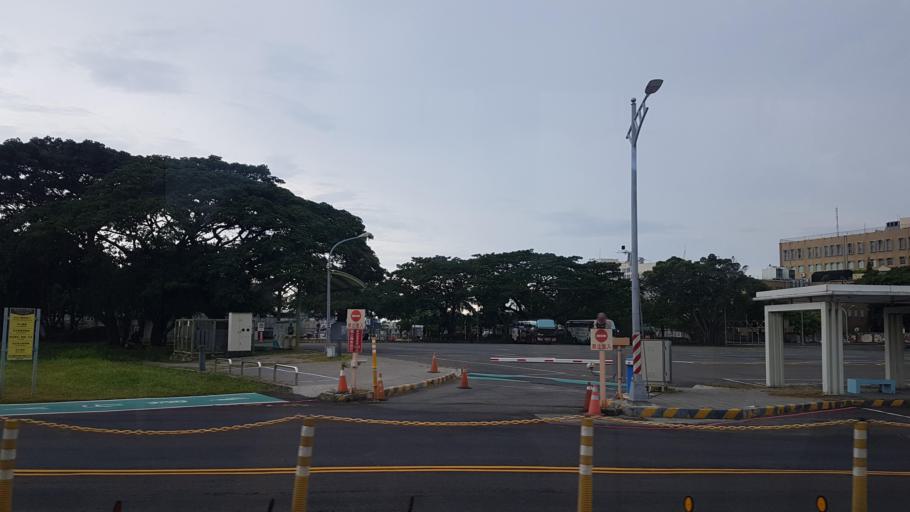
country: TW
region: Kaohsiung
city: Kaohsiung
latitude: 22.6205
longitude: 120.2767
